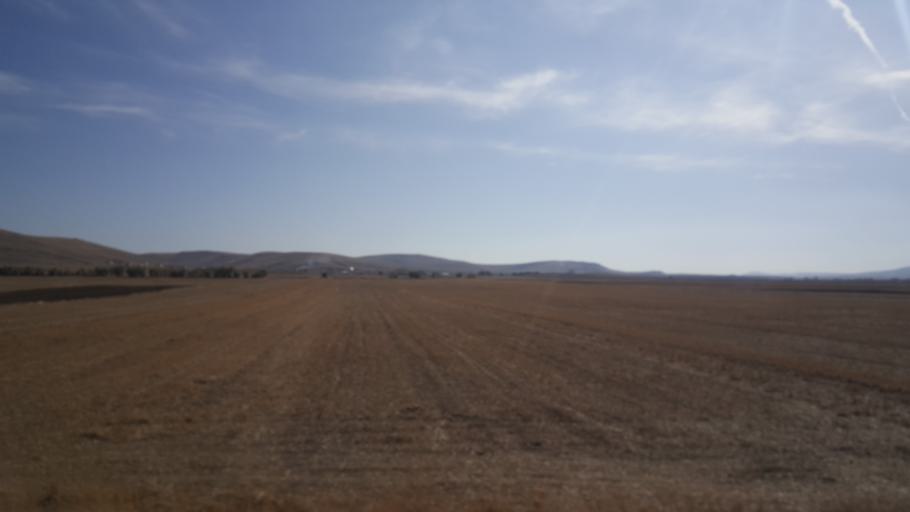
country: TR
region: Ankara
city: Yenice
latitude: 39.3824
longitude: 32.8080
